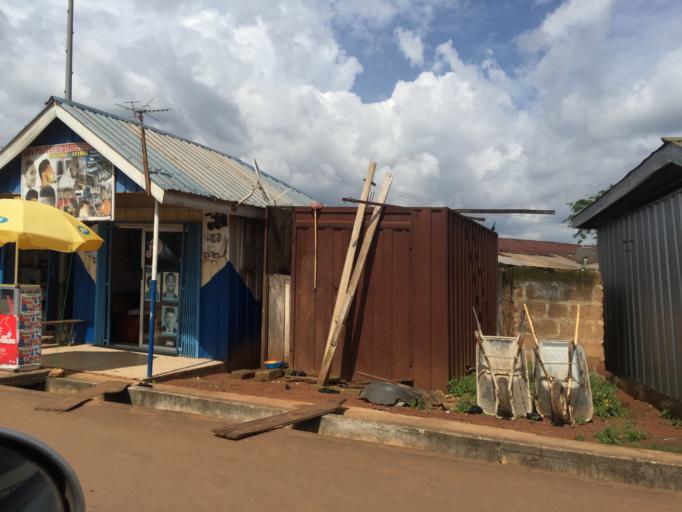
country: GH
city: Mpraeso
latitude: 6.5885
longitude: -0.7362
